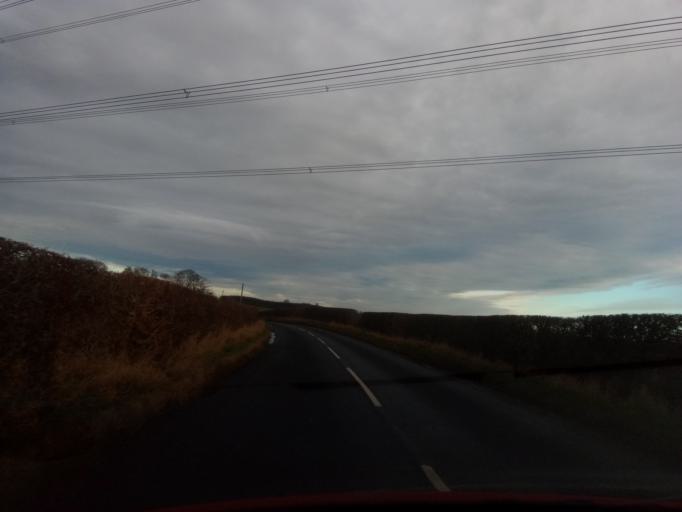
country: GB
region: Scotland
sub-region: The Scottish Borders
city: Coldstream
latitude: 55.6714
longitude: -2.2279
